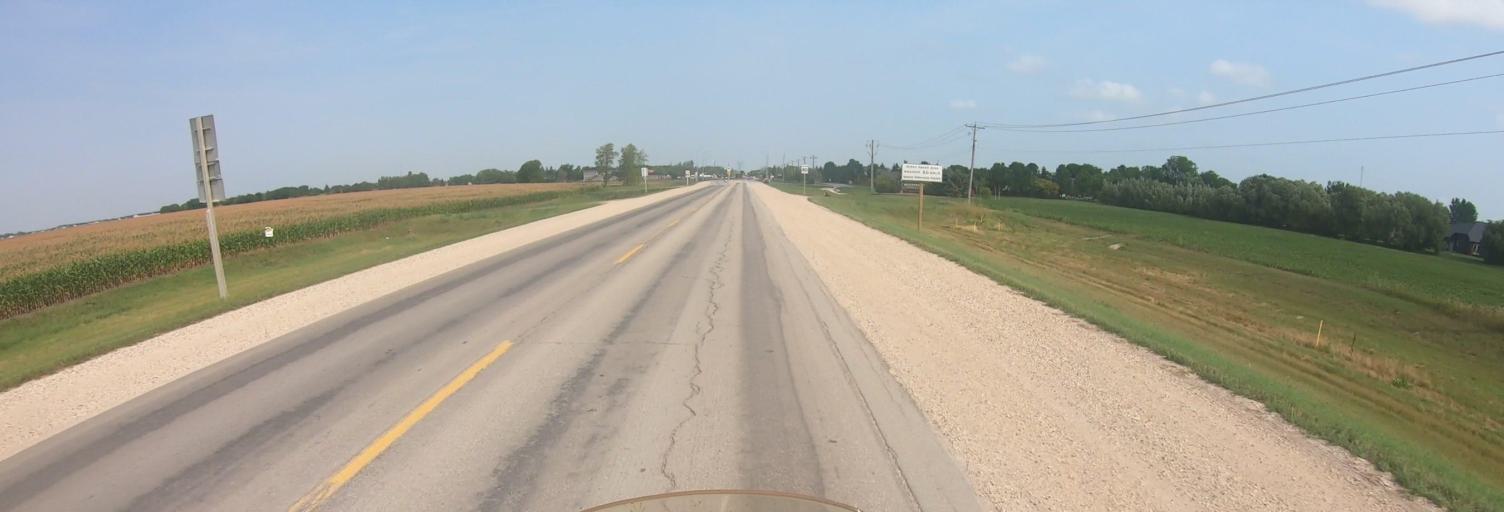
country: CA
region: Manitoba
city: Steinbach
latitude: 49.5070
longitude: -96.6912
